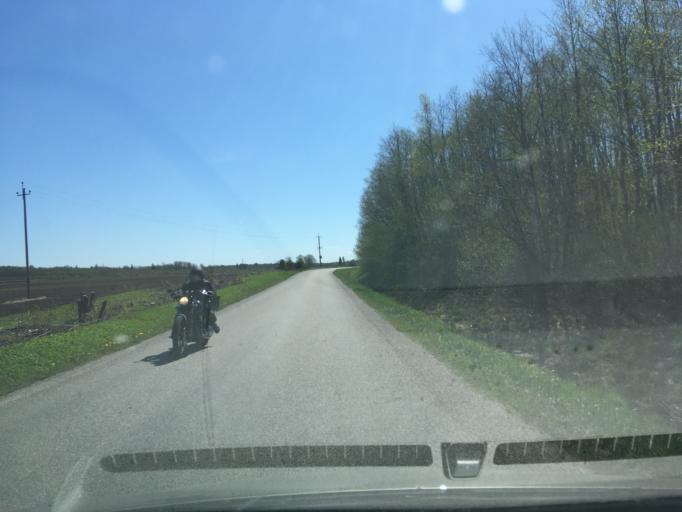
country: EE
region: Harju
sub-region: Raasiku vald
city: Arukula
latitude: 59.4005
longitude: 25.0792
